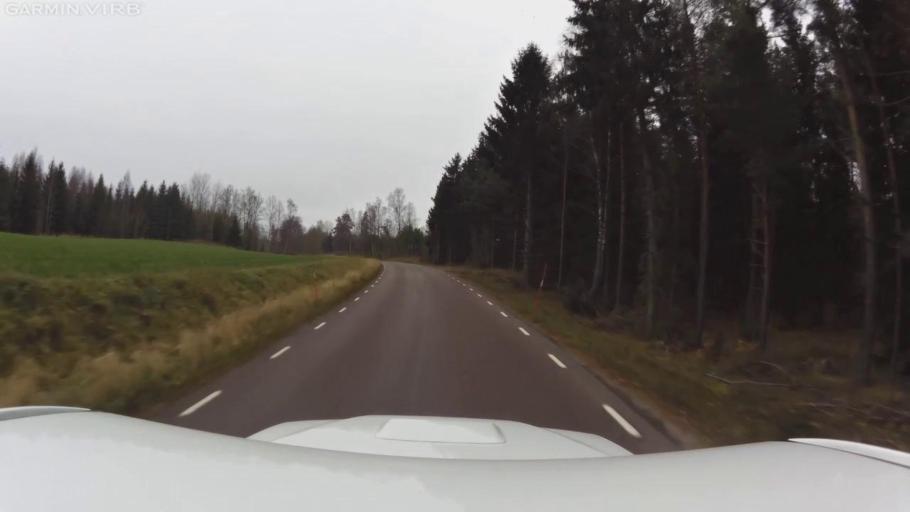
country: SE
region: OEstergoetland
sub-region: Mjolby Kommun
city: Mantorp
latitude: 58.1607
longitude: 15.3916
